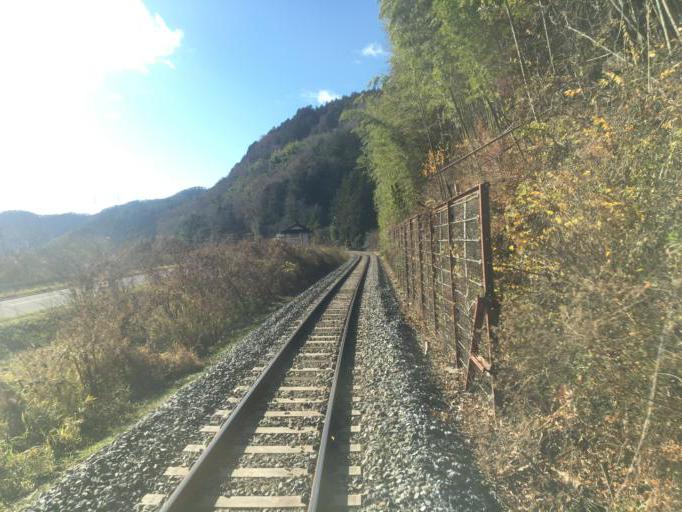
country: JP
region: Iwate
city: Ichinoseki
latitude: 38.9532
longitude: 141.2488
